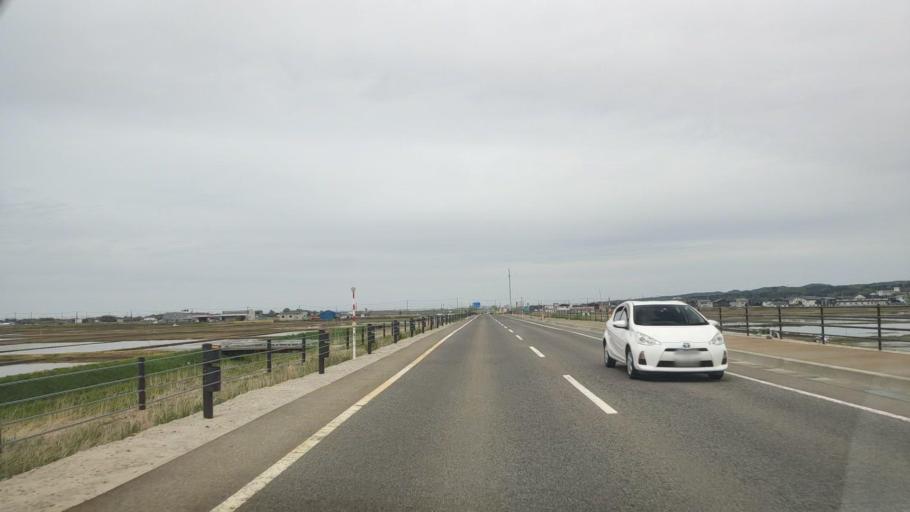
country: JP
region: Niigata
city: Shirone
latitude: 37.7468
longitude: 139.0845
